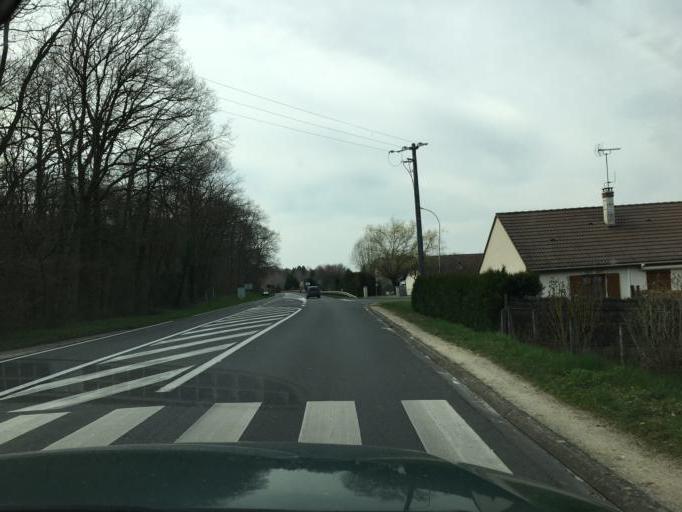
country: FR
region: Centre
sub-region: Departement du Loiret
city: Vienne-en-Val
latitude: 47.8014
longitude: 2.1292
